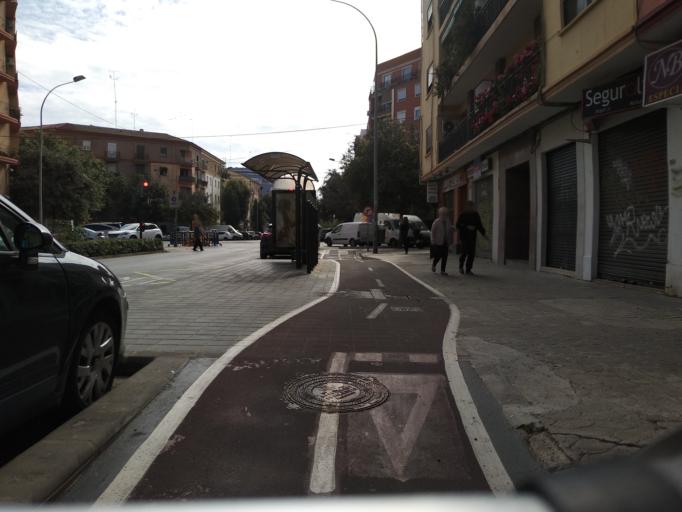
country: ES
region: Valencia
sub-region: Provincia de Valencia
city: Tavernes Blanques
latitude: 39.4849
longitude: -0.3698
